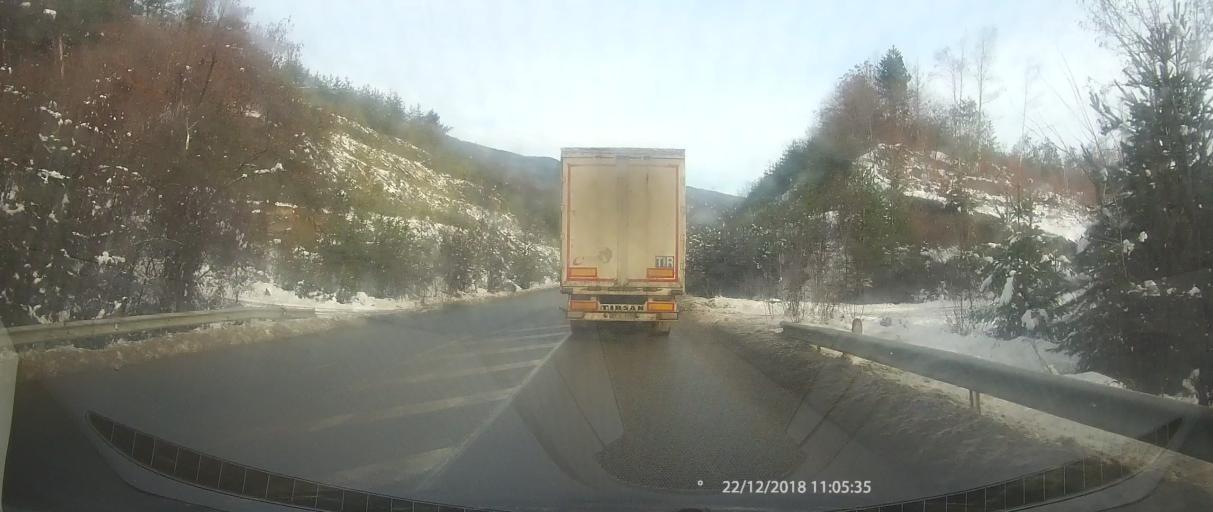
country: BG
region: Kyustendil
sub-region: Obshtina Kyustendil
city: Kyustendil
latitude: 42.2647
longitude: 22.5774
